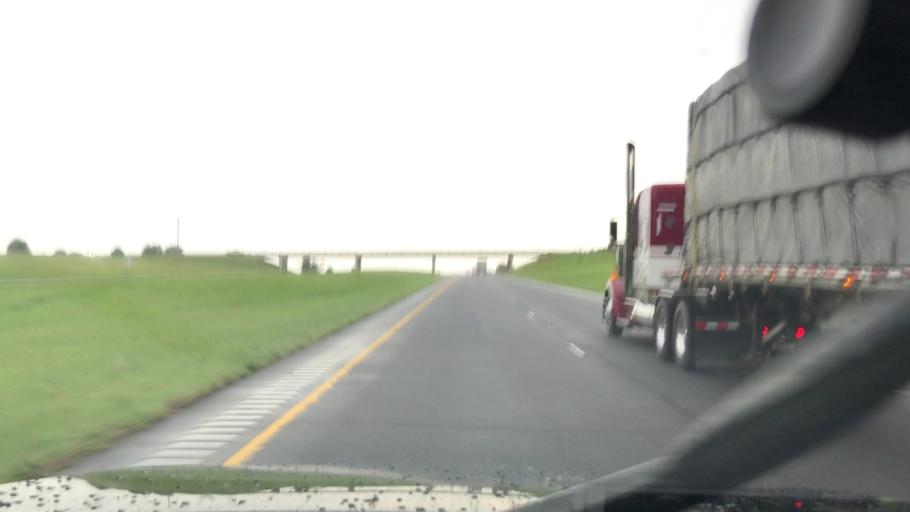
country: US
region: North Carolina
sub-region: Iredell County
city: Statesville
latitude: 35.9147
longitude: -80.8543
